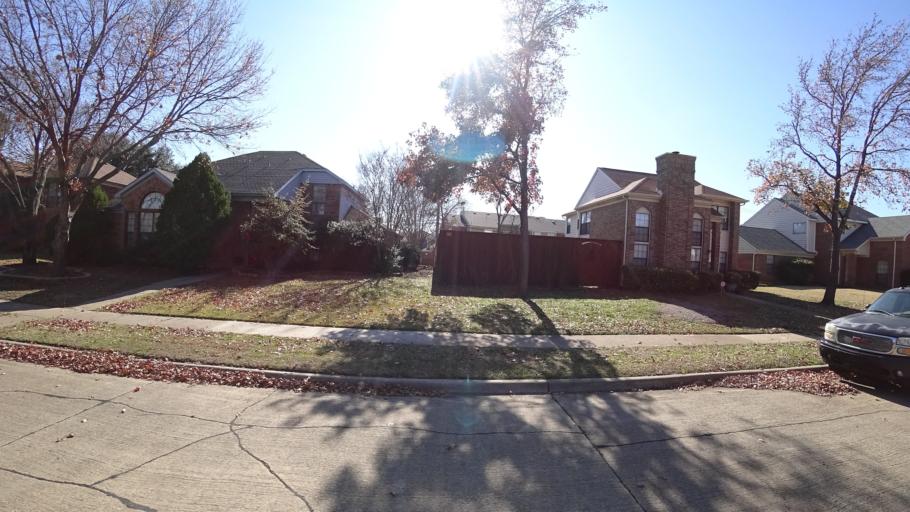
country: US
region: Texas
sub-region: Denton County
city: Lewisville
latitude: 33.0067
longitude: -97.0000
